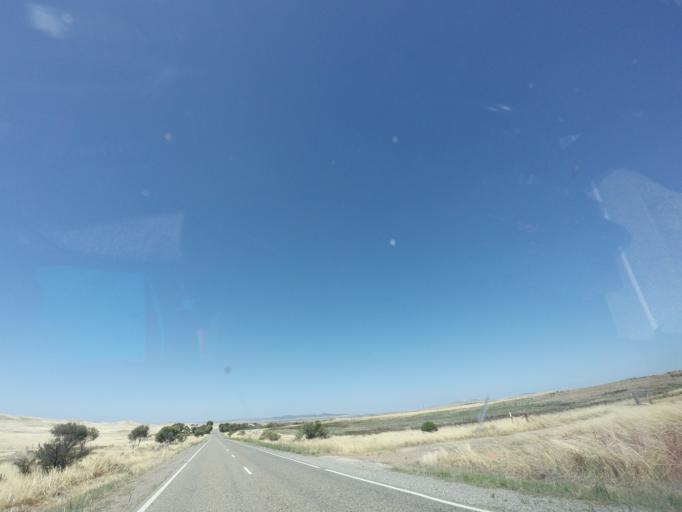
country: AU
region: South Australia
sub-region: Peterborough
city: Peterborough
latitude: -32.7401
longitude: 138.5776
